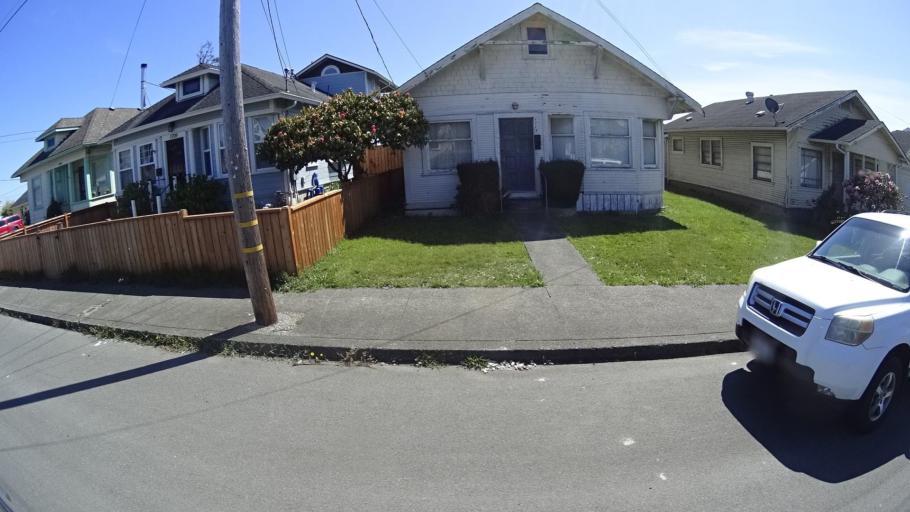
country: US
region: California
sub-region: Humboldt County
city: Eureka
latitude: 40.7934
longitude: -124.1482
